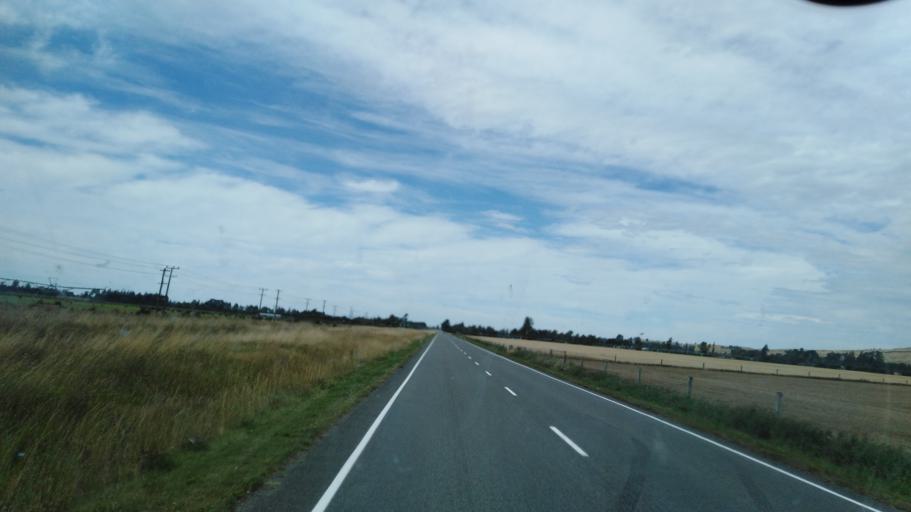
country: NZ
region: Canterbury
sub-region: Selwyn District
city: Darfield
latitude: -43.3664
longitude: 171.9808
